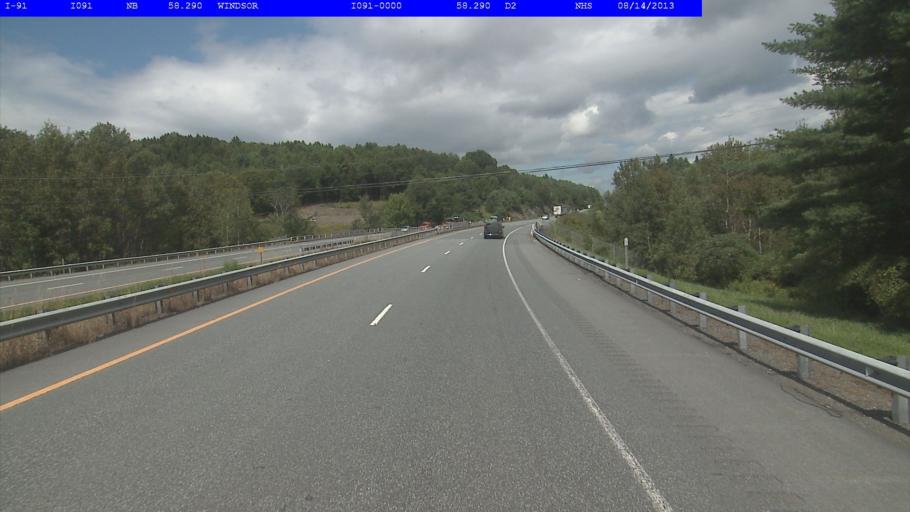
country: US
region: Vermont
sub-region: Windsor County
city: Windsor
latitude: 43.4988
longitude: -72.4108
